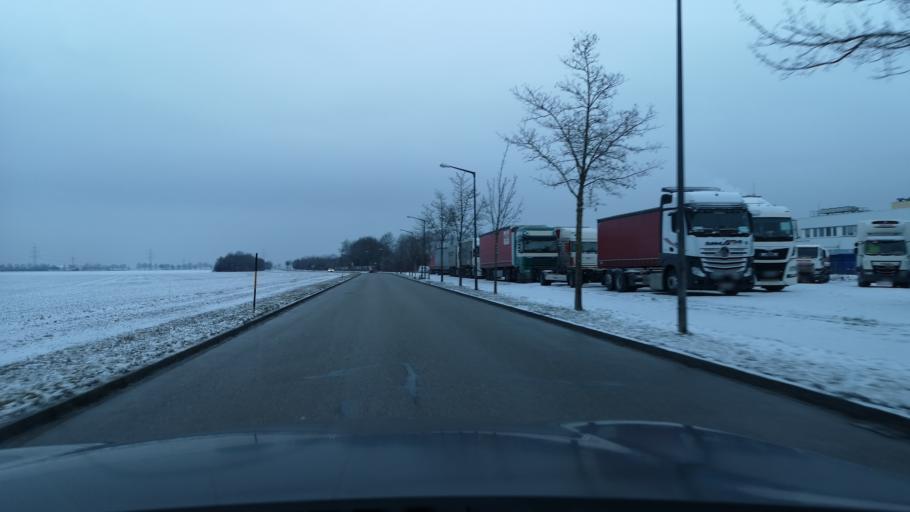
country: DE
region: Bavaria
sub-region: Upper Bavaria
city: Poing
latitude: 48.1697
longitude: 11.7916
